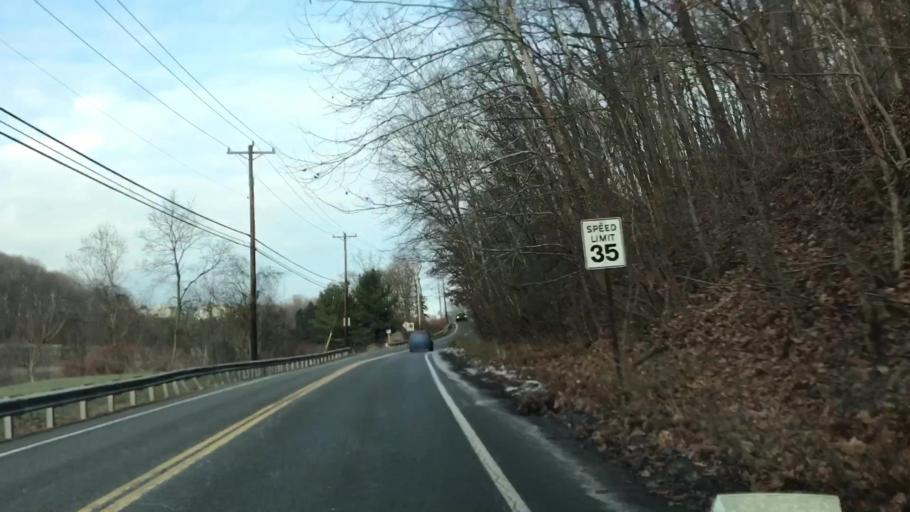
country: US
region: Pennsylvania
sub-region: Allegheny County
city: Ben Avon
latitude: 40.5387
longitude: -80.0768
